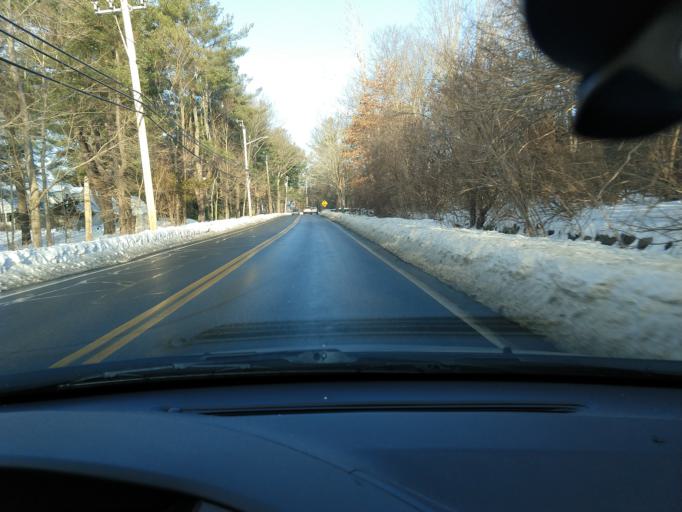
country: US
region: Massachusetts
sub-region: Middlesex County
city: Concord
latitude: 42.4721
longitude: -71.3631
